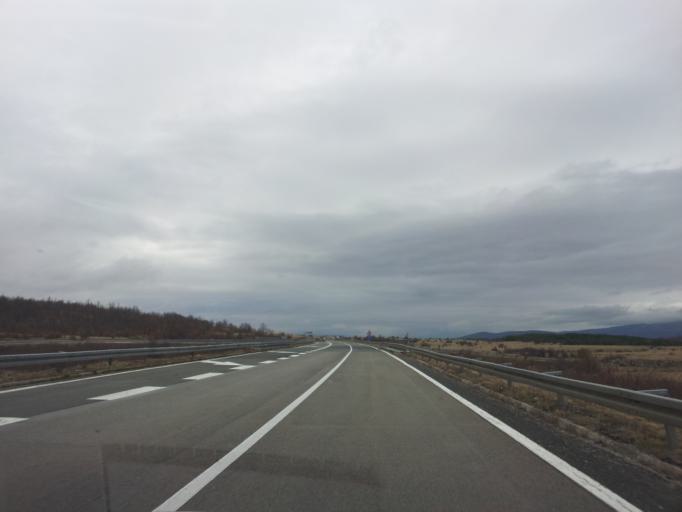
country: HR
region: Zadarska
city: Gracac
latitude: 44.5069
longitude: 15.7466
